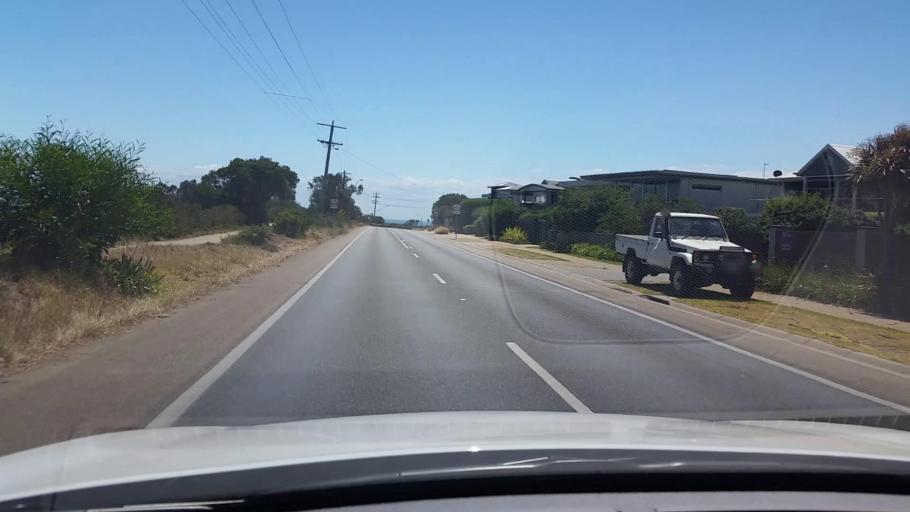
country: AU
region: Victoria
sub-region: Mornington Peninsula
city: Mornington
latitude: -38.2315
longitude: 145.0268
